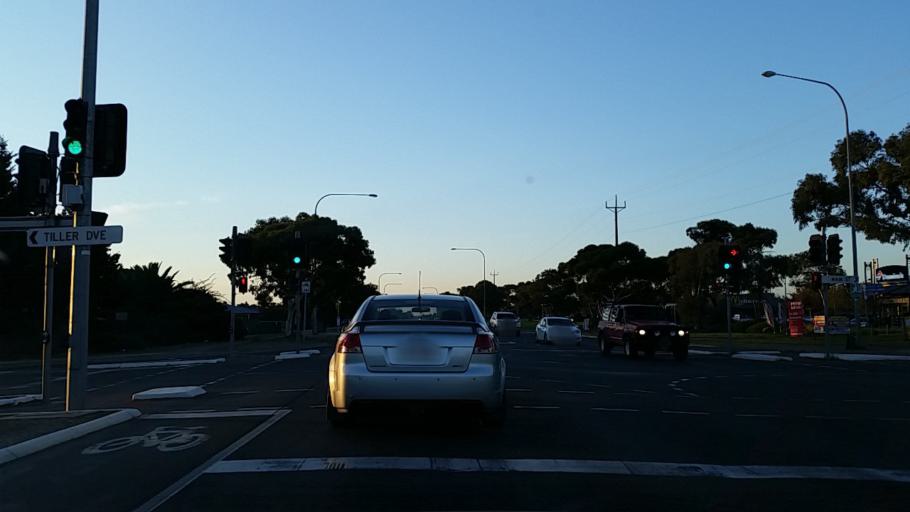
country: AU
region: South Australia
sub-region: Onkaparinga
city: Seaford
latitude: -35.1873
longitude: 138.4772
